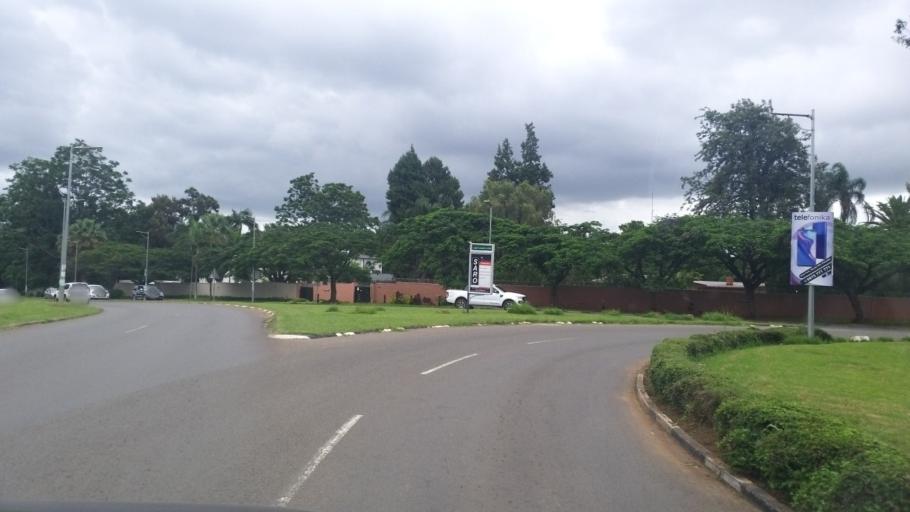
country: ZM
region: Lusaka
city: Lusaka
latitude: -15.4233
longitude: 28.3341
